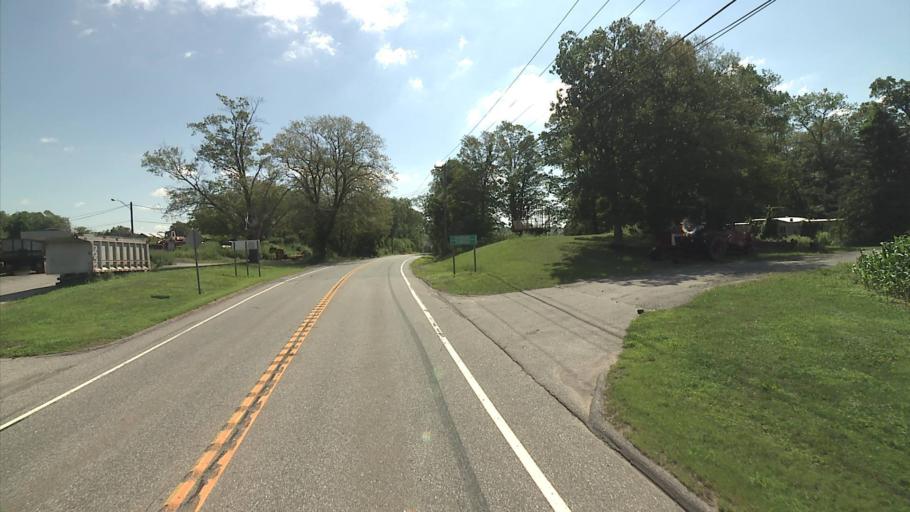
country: US
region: Connecticut
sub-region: New London County
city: Baltic
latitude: 41.6988
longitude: -72.0676
